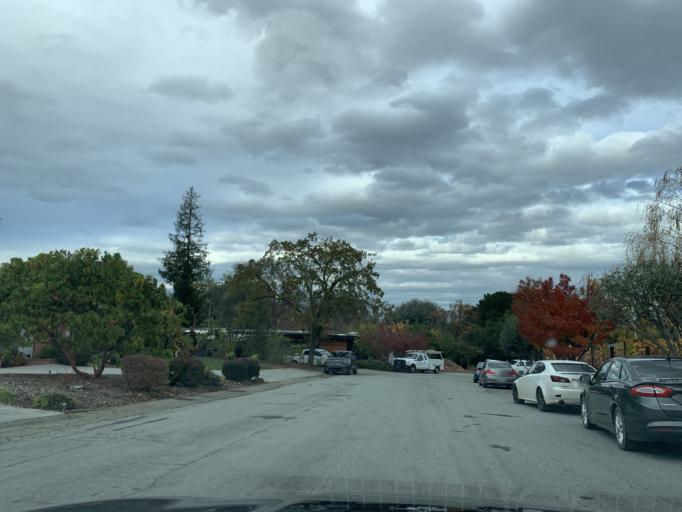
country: US
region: California
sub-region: Santa Clara County
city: Monte Sereno
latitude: 37.2574
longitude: -121.9752
